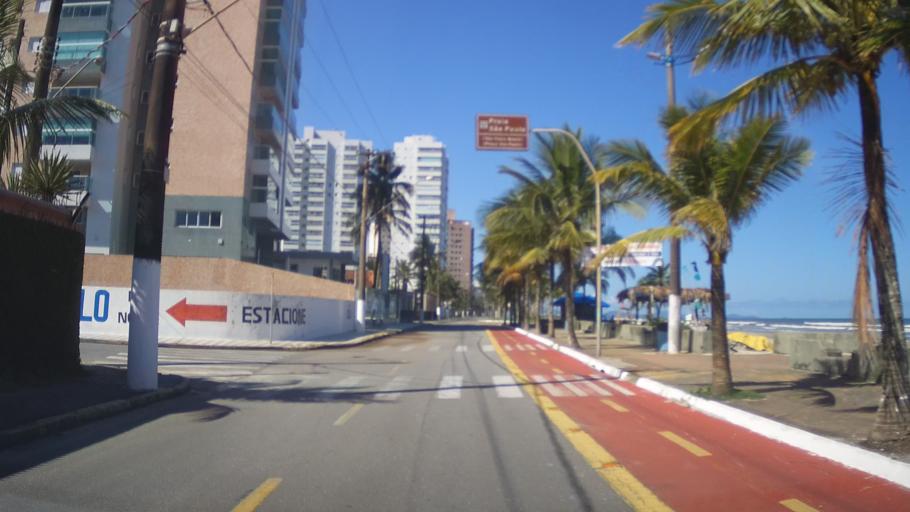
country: BR
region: Sao Paulo
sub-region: Mongagua
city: Mongagua
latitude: -24.0893
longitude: -46.6065
